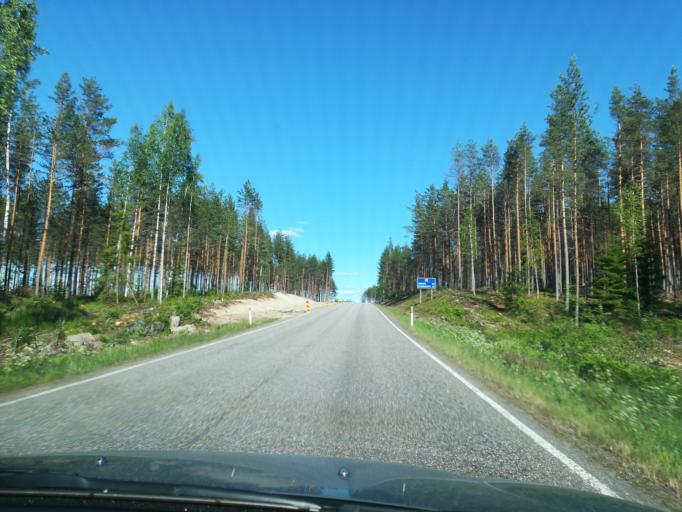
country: FI
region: Southern Savonia
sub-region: Mikkeli
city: Puumala
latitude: 61.4640
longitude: 28.3391
